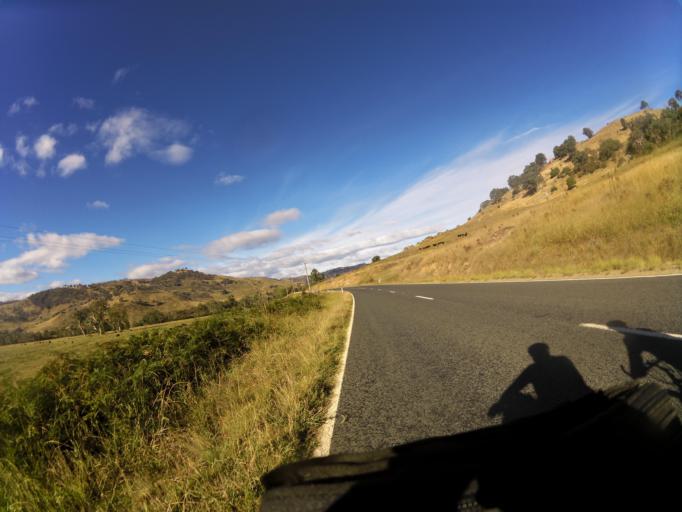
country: AU
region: New South Wales
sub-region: Greater Hume Shire
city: Holbrook
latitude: -35.9656
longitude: 147.7607
